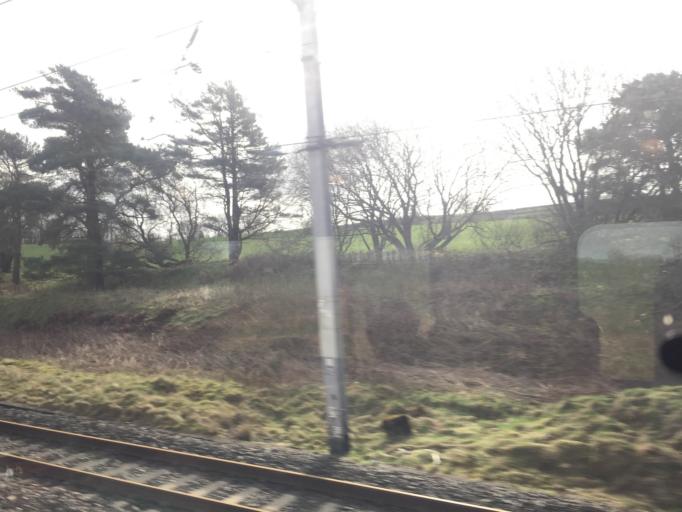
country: GB
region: England
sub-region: Cumbria
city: Sedbergh
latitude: 54.3588
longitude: -2.6171
